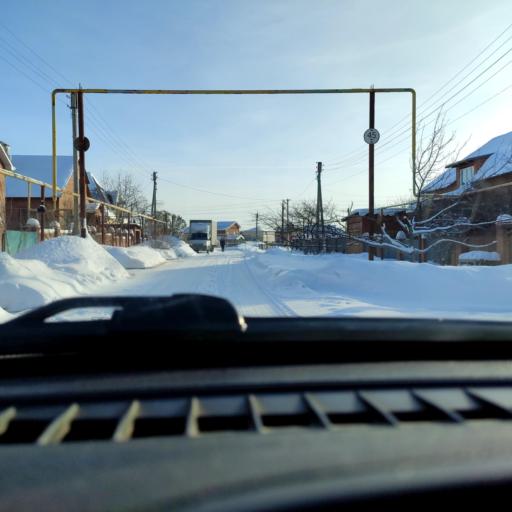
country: RU
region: Samara
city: Podstepki
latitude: 53.5116
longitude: 49.1874
